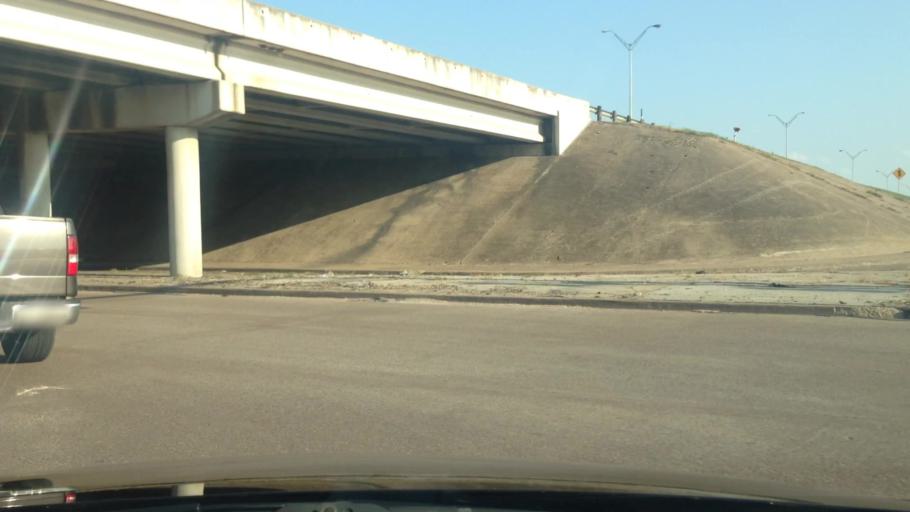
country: US
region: Texas
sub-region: Tarrant County
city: Everman
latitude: 32.6276
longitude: -97.3220
